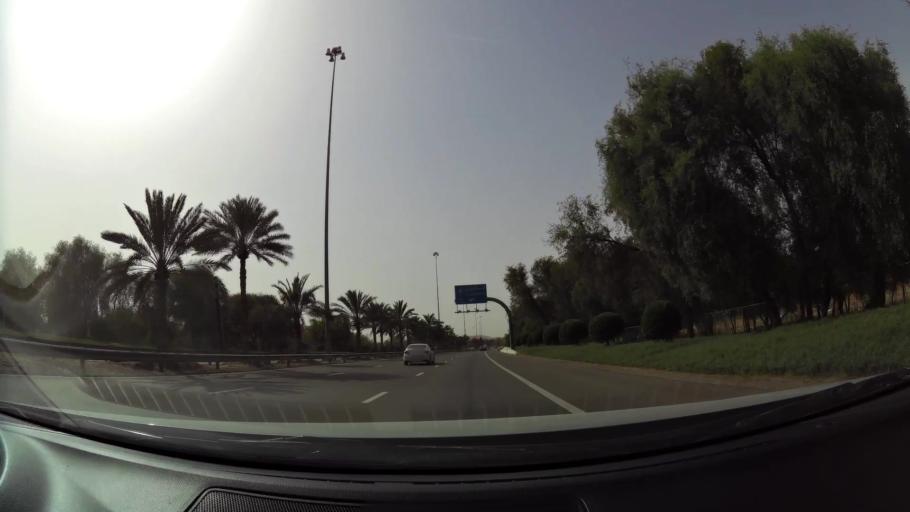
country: AE
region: Abu Dhabi
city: Al Ain
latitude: 24.1912
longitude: 55.5910
